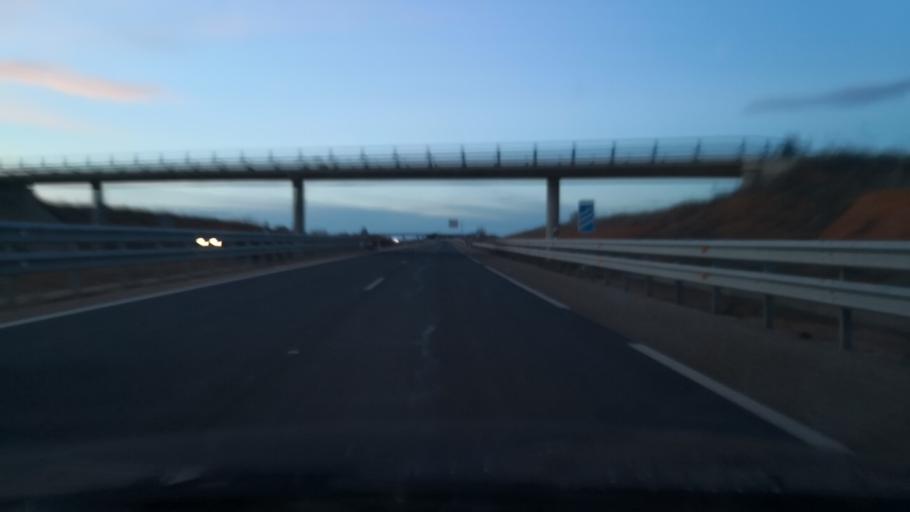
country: ES
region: Castille and Leon
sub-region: Provincia de Zamora
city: Morales de Toro
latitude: 41.5342
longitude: -5.2825
